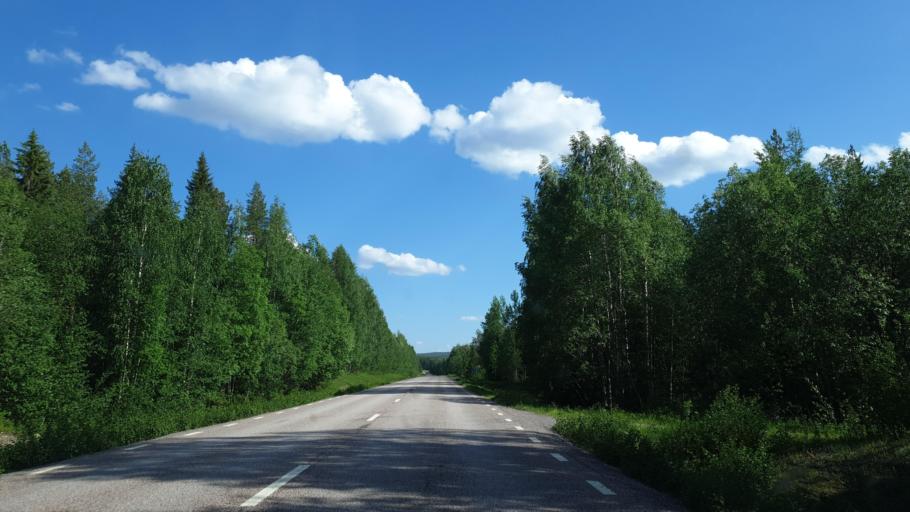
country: SE
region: Norrbotten
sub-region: Alvsbyns Kommun
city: AElvsbyn
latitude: 65.7940
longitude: 20.6537
